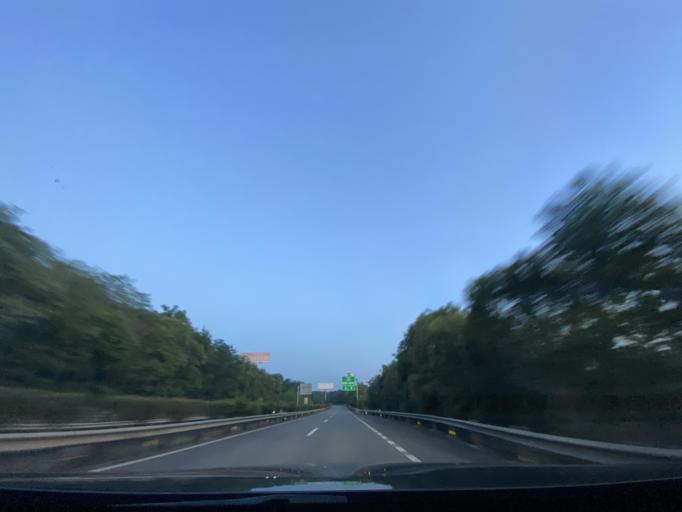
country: CN
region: Sichuan
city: Longquan
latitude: 30.4843
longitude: 104.4005
